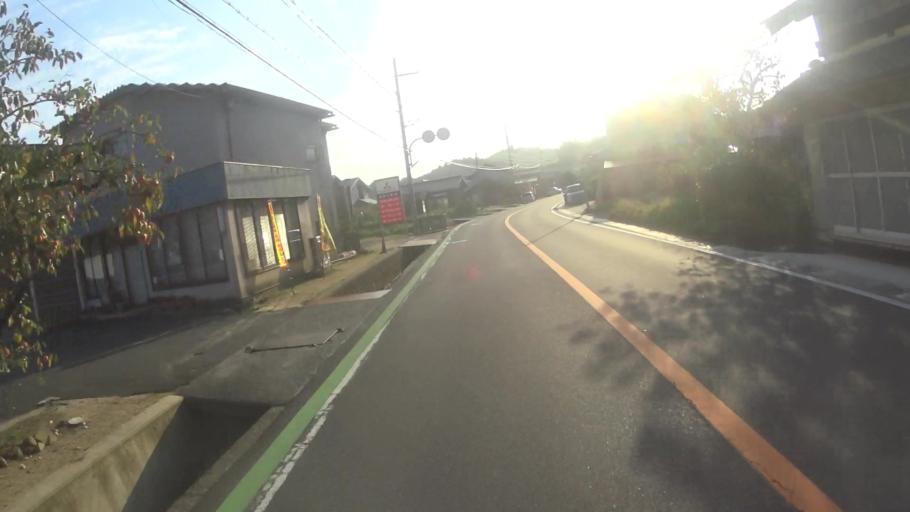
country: JP
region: Kyoto
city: Miyazu
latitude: 35.6338
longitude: 135.0768
